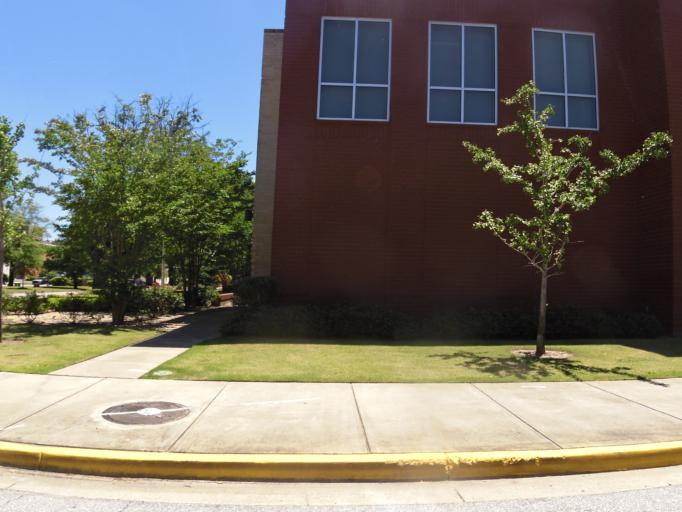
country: US
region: Georgia
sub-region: Richmond County
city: Augusta
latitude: 33.4737
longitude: -81.9685
